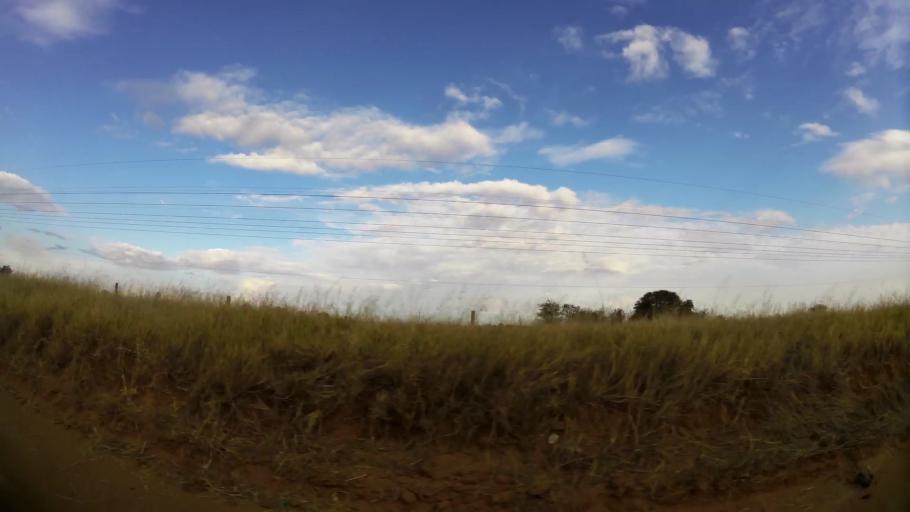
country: ZA
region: Orange Free State
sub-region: Lejweleputswa District Municipality
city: Welkom
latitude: -28.0137
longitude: 26.7231
